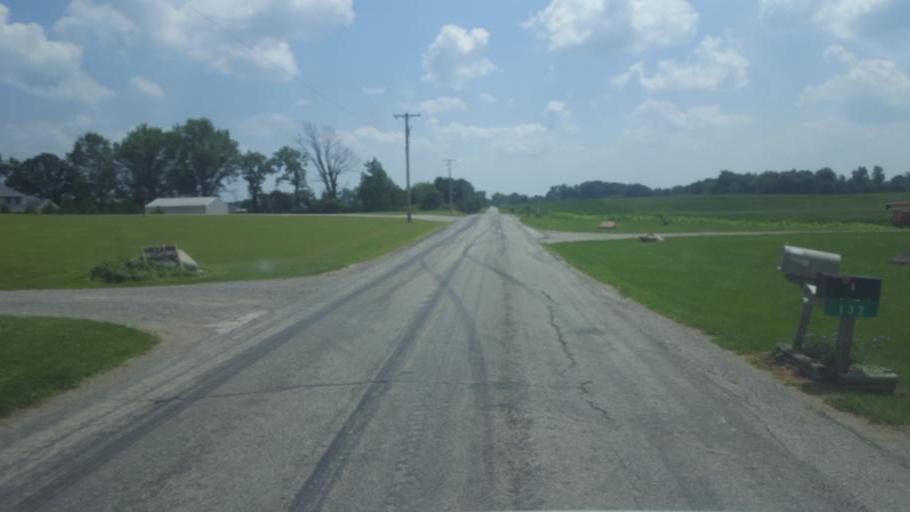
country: US
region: Ohio
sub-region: Crawford County
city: Crestline
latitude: 40.7552
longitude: -82.6983
